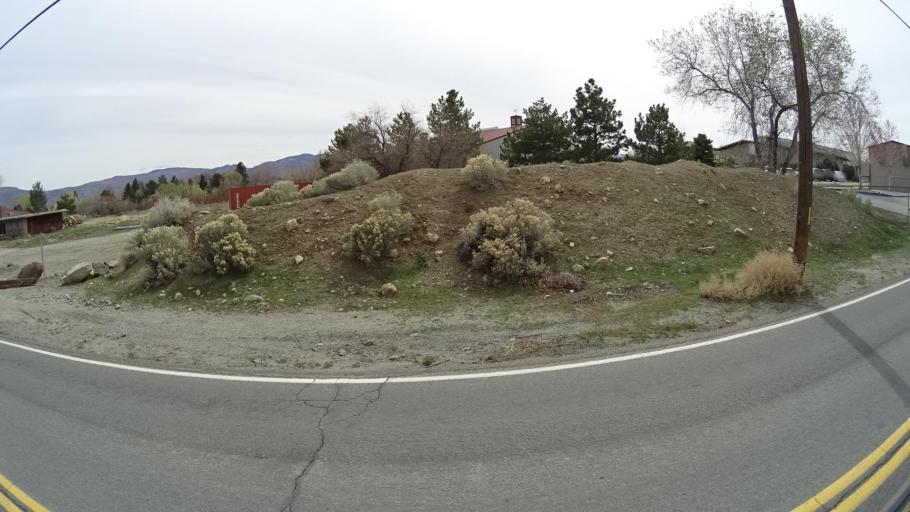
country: US
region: Nevada
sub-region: Washoe County
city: Reno
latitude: 39.4333
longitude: -119.7751
